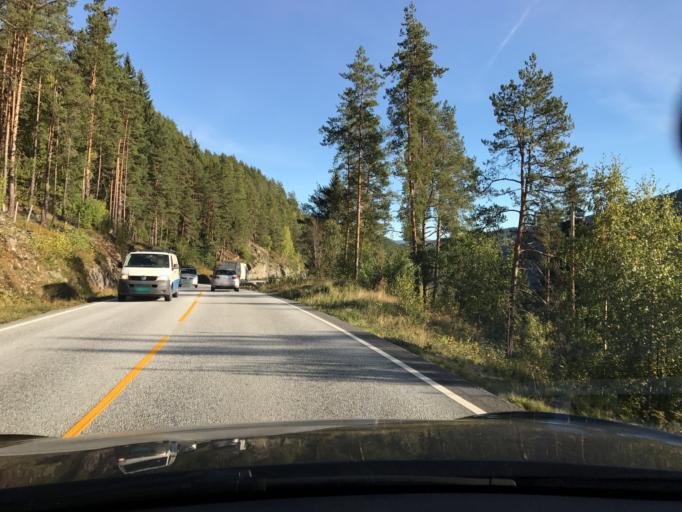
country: NO
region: Sogn og Fjordane
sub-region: Sogndal
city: Sogndalsfjora
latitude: 61.2114
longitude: 7.1463
